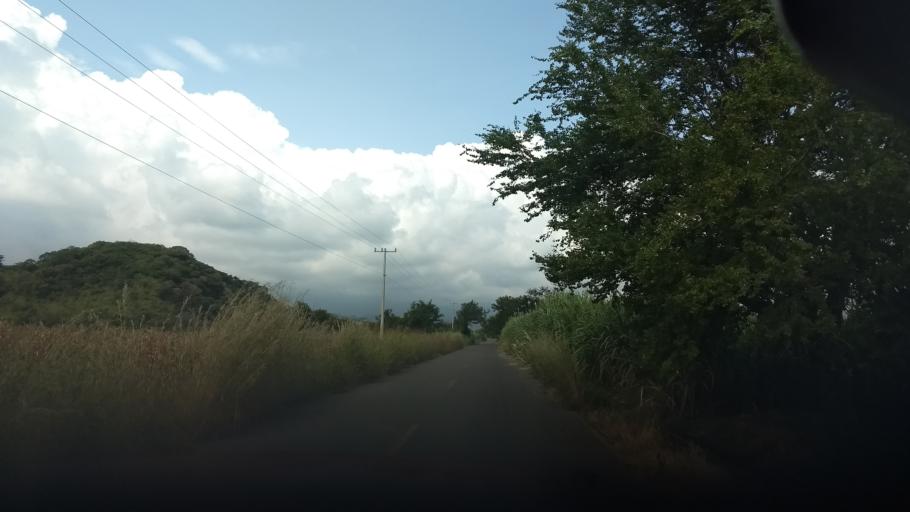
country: MX
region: Jalisco
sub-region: Tonila
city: San Marcos
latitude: 19.4233
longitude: -103.4903
